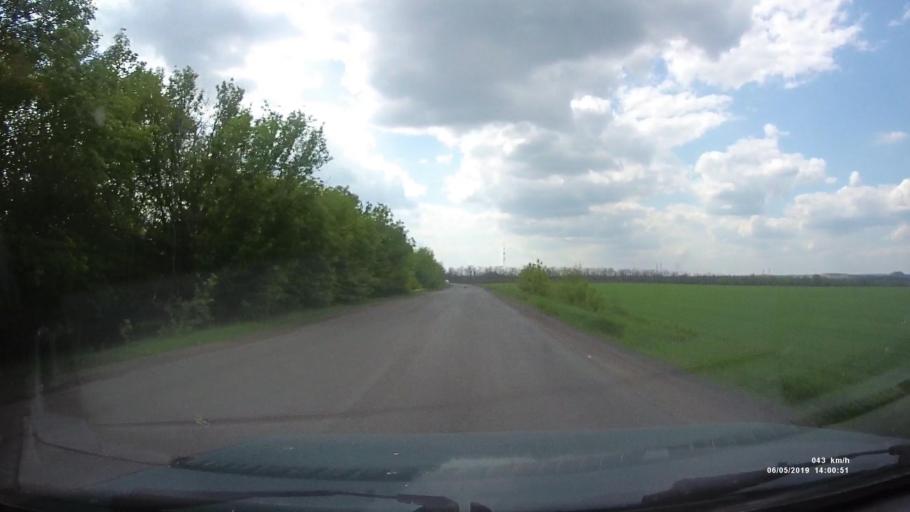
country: RU
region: Rostov
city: Shakhty
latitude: 47.6858
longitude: 40.3828
